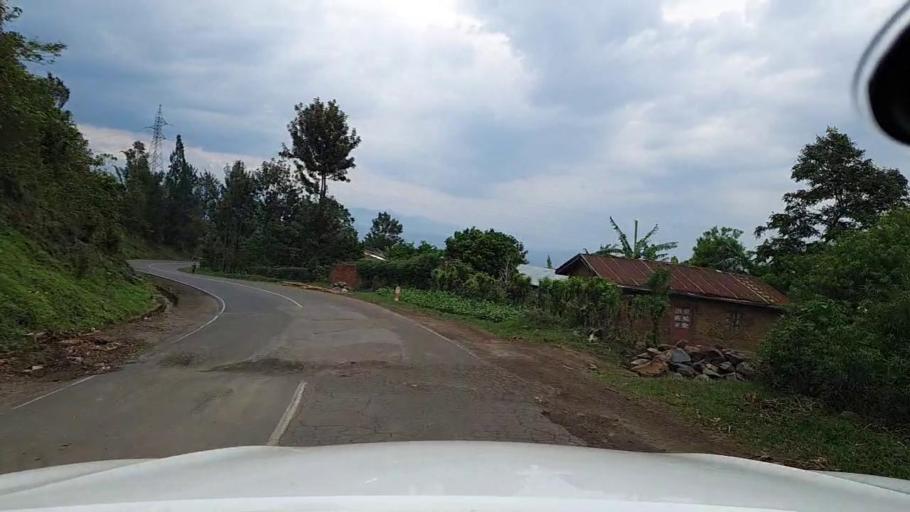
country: RW
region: Western Province
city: Cyangugu
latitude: -2.6597
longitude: 28.9733
